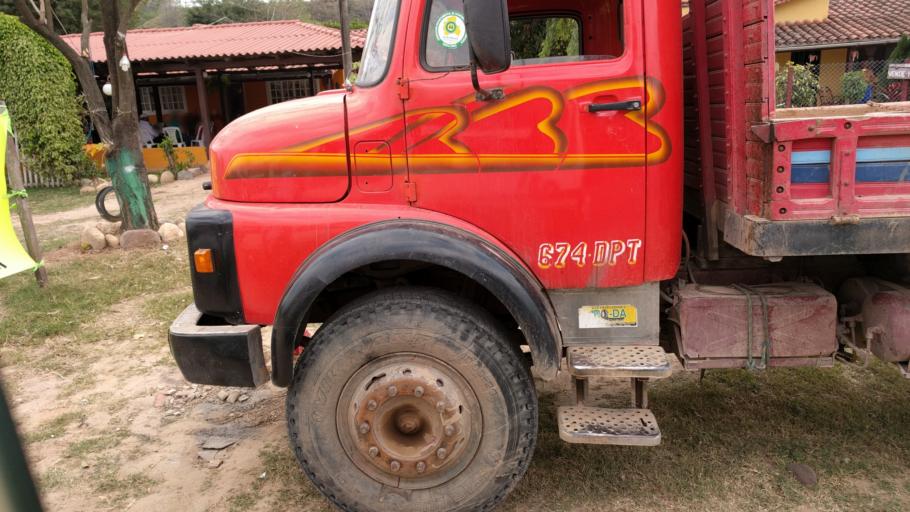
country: BO
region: Santa Cruz
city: Jorochito
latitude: -18.1214
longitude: -63.4632
